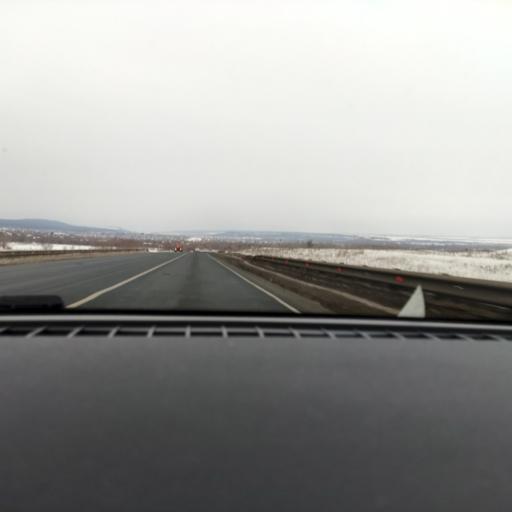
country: RU
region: Samara
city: Novosemeykino
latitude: 53.4072
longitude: 50.3627
